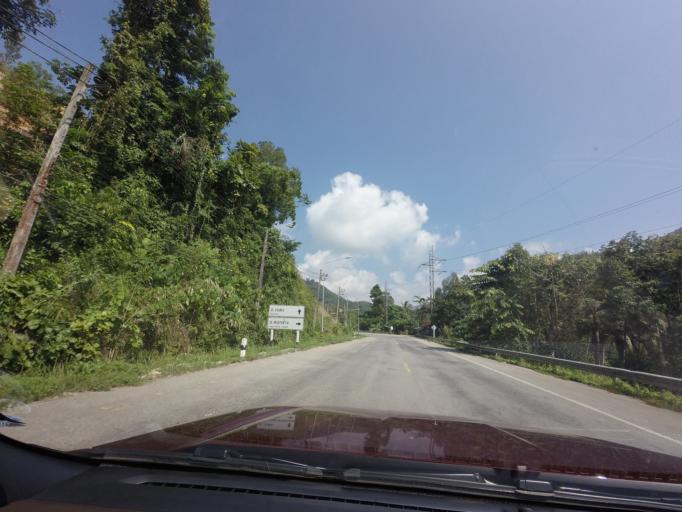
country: TH
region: Yala
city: Betong
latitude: 5.9214
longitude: 101.1641
